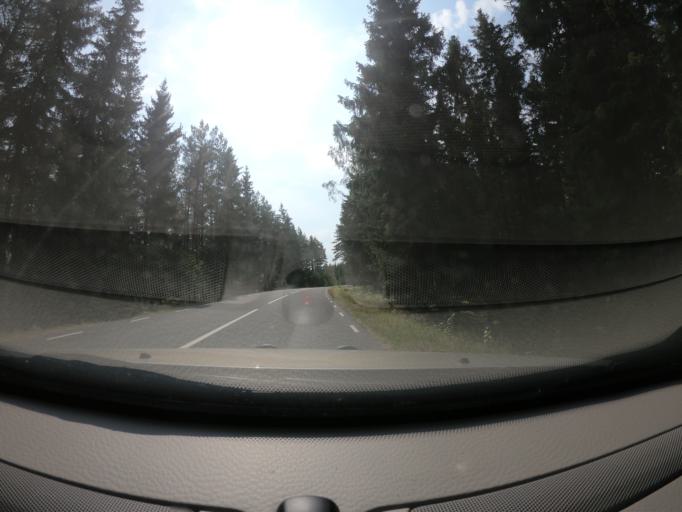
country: SE
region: Joenkoeping
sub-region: Vetlanda Kommun
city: Landsbro
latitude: 57.2509
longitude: 14.9454
